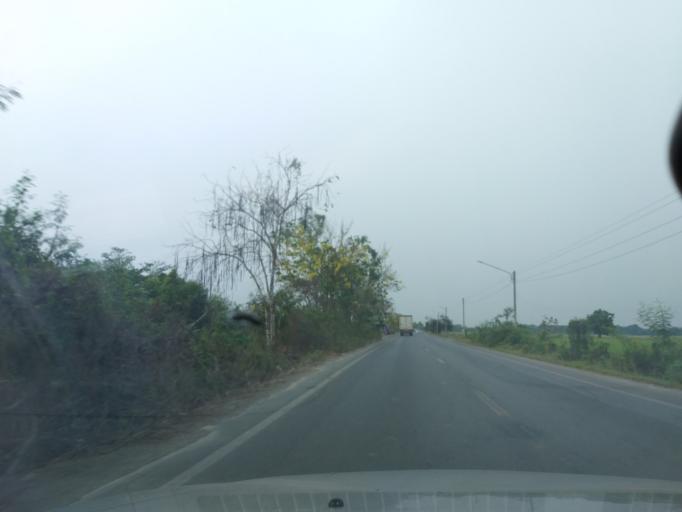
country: TH
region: Bangkok
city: Nong Chok
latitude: 13.9493
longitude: 100.8948
